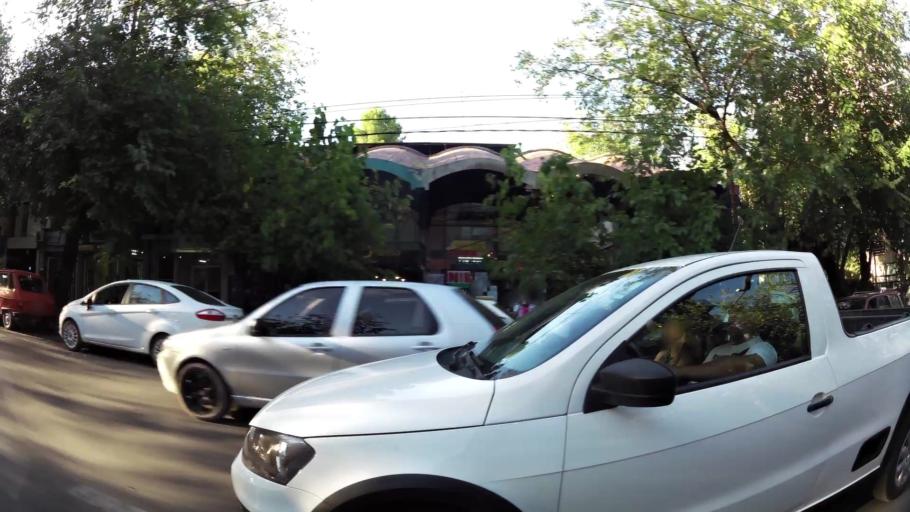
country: AR
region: Mendoza
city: Mendoza
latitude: -32.8942
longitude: -68.8446
